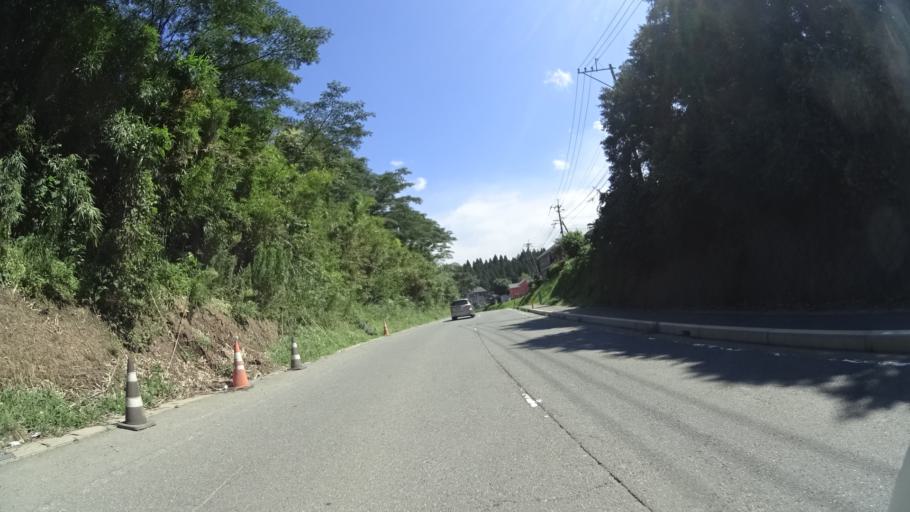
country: JP
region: Kumamoto
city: Aso
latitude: 32.8822
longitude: 131.0022
